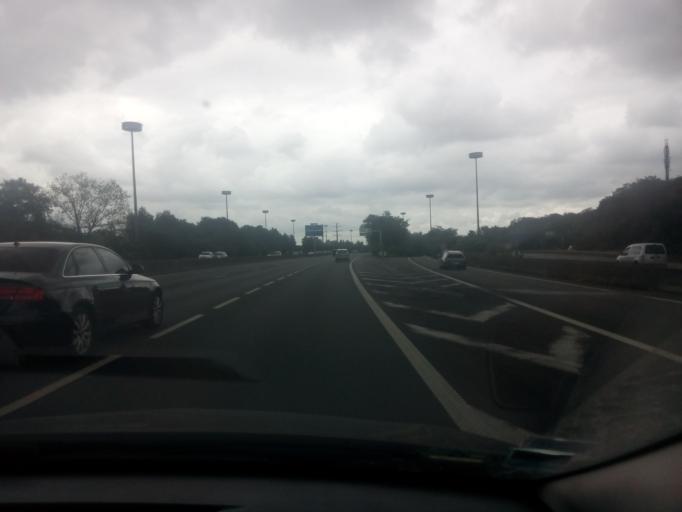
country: FR
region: Ile-de-France
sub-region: Departement du Val-de-Marne
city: Chevilly-Larue
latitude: 48.7700
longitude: 2.3450
